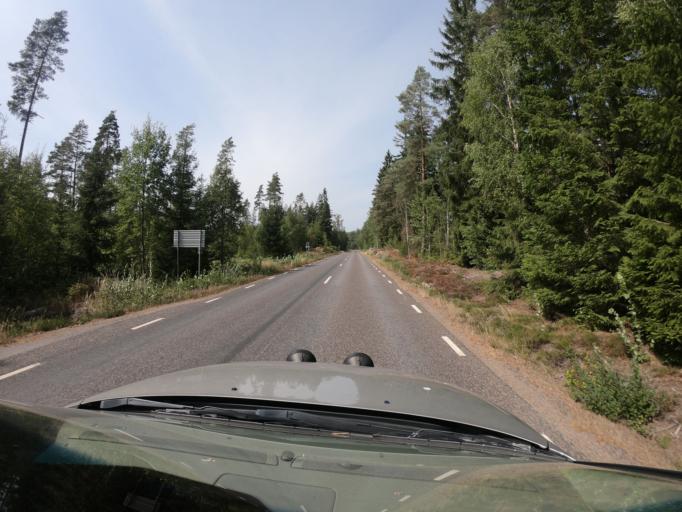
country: SE
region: Kronoberg
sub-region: Vaxjo Kommun
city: Braas
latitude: 57.0609
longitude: 15.0338
